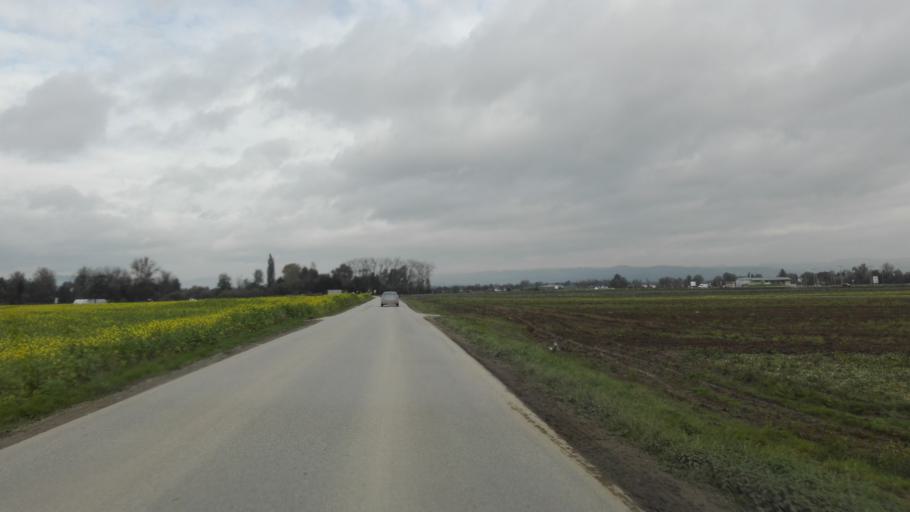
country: AT
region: Upper Austria
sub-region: Politischer Bezirk Urfahr-Umgebung
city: Feldkirchen an der Donau
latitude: 48.3135
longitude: 14.0038
